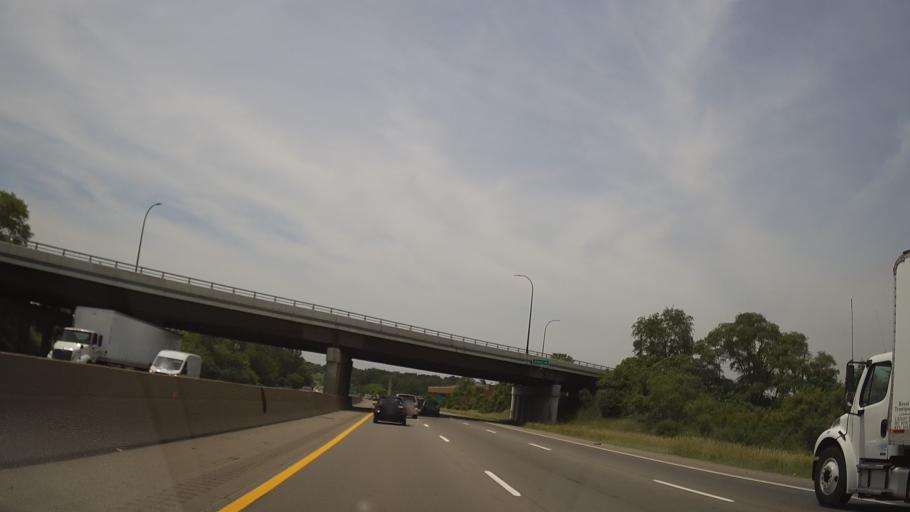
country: US
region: Michigan
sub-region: Washtenaw County
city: Ypsilanti
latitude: 42.2316
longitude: -83.5989
